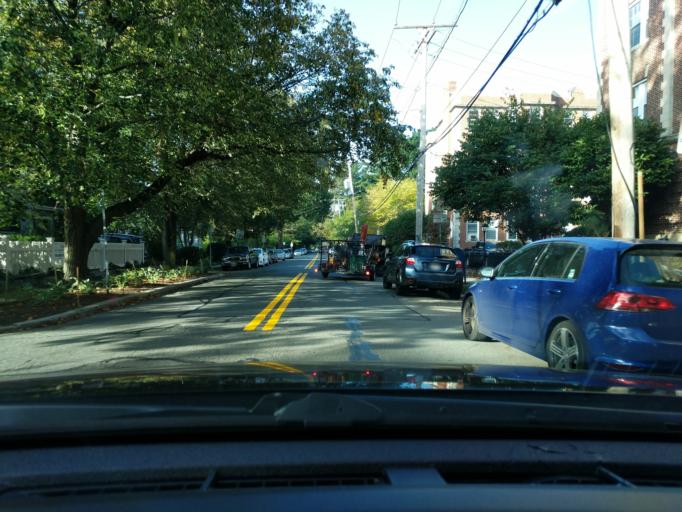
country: US
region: Massachusetts
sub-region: Middlesex County
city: Cambridge
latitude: 42.3791
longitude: -71.1268
